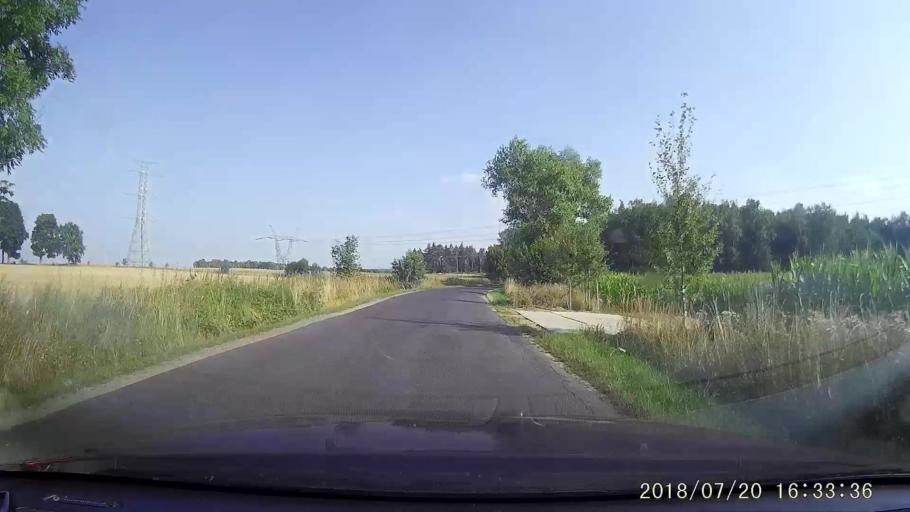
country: PL
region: Lower Silesian Voivodeship
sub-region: Powiat zgorzelecki
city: Sulikow
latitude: 51.0885
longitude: 15.0969
